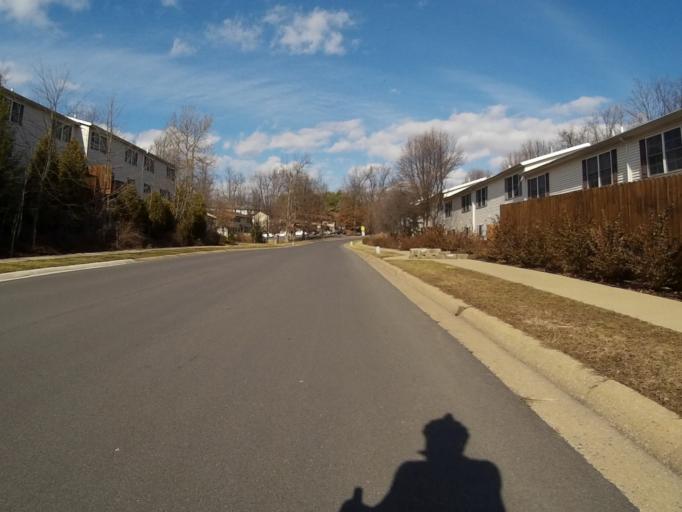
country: US
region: Pennsylvania
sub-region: Centre County
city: Park Forest Village
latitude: 40.8066
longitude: -77.9236
